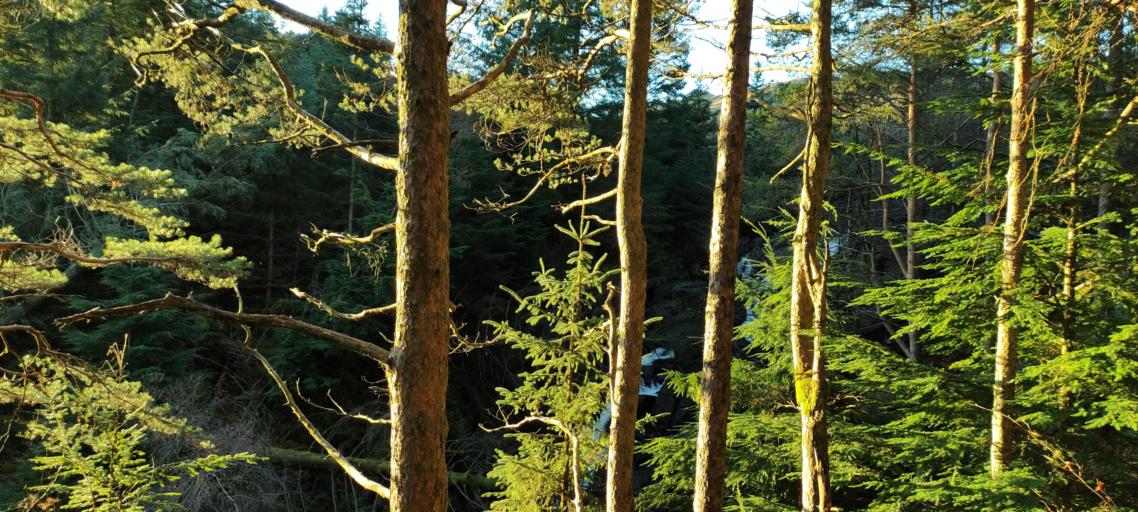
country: GB
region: England
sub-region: Cumbria
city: Keswick
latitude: 54.5147
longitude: -3.0612
